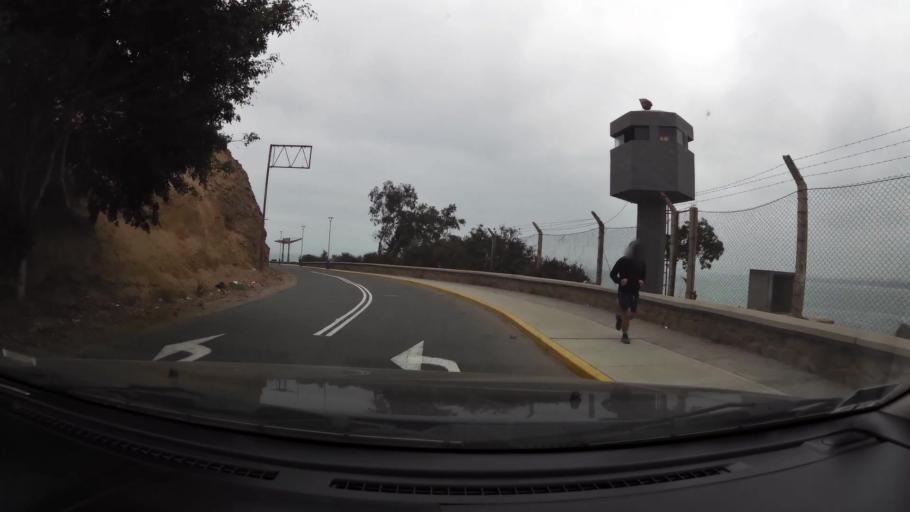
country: PE
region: Lima
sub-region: Lima
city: Surco
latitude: -12.1670
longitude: -77.0342
